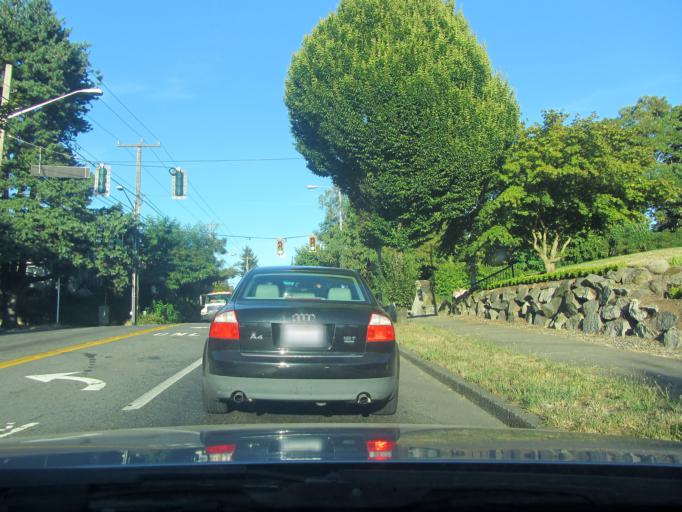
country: US
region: Washington
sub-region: King County
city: Seattle
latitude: 47.6650
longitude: -122.3341
